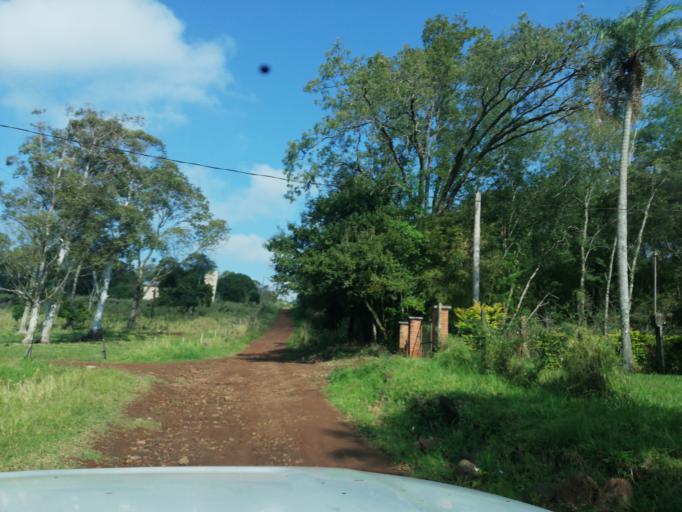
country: AR
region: Misiones
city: Cerro Azul
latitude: -27.6035
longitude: -55.5351
